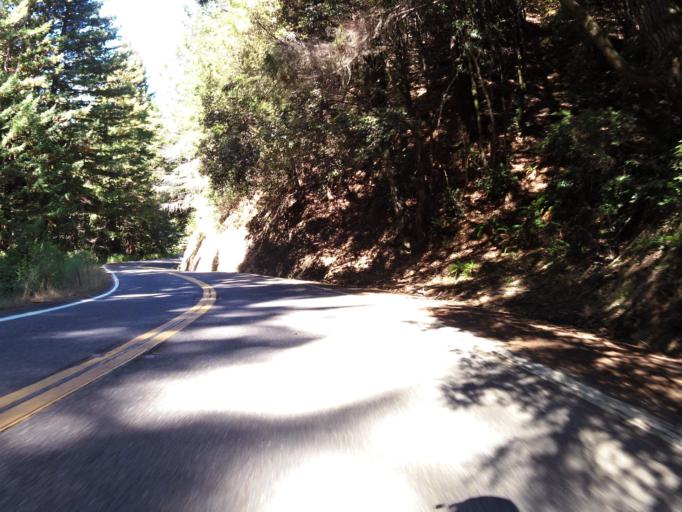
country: US
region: California
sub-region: Humboldt County
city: Redway
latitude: 39.7956
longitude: -123.8160
